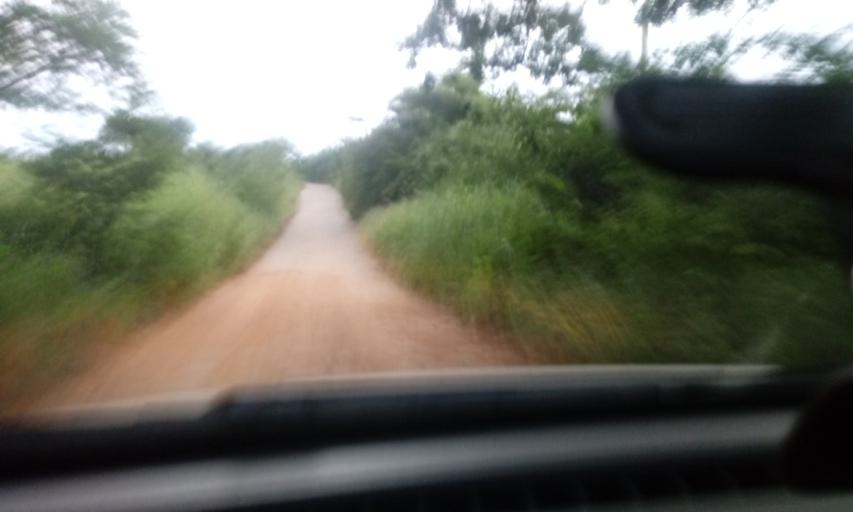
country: BR
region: Bahia
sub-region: Riacho De Santana
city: Riacho de Santana
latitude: -13.8000
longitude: -42.7450
